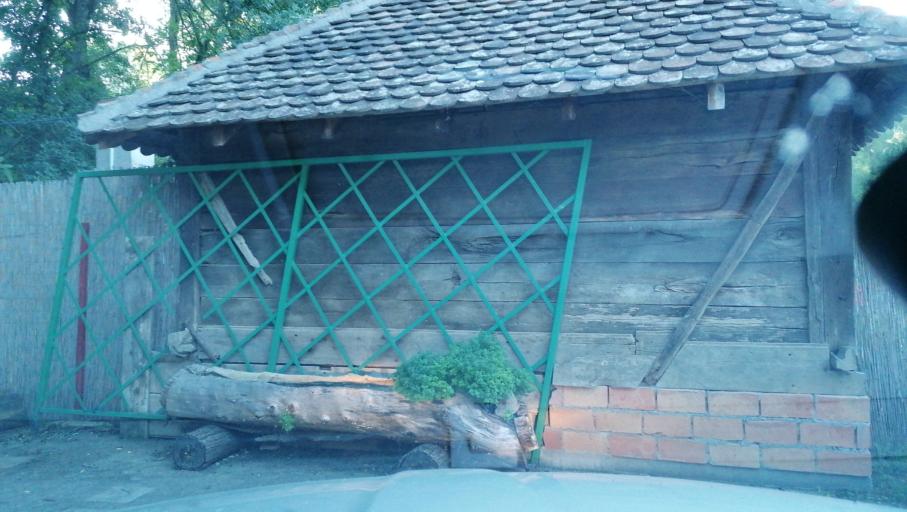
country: RS
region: Central Serbia
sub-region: Sumadijski Okrug
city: Topola
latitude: 44.2646
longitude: 20.6693
